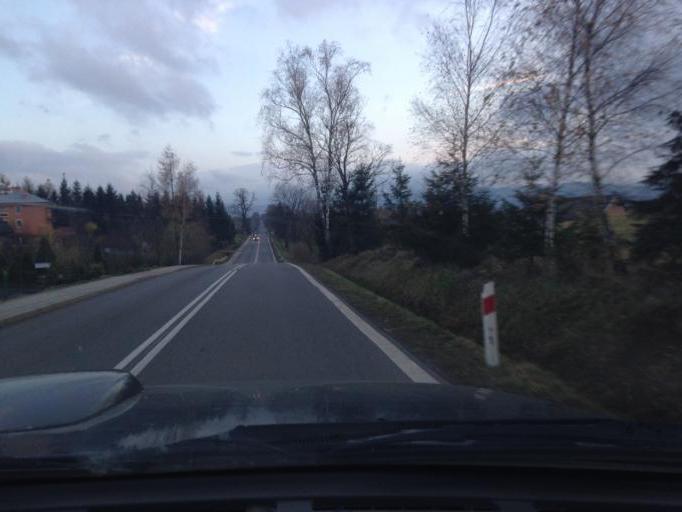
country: PL
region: Subcarpathian Voivodeship
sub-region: Powiat jasielski
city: Nowy Zmigrod
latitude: 49.6374
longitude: 21.5236
